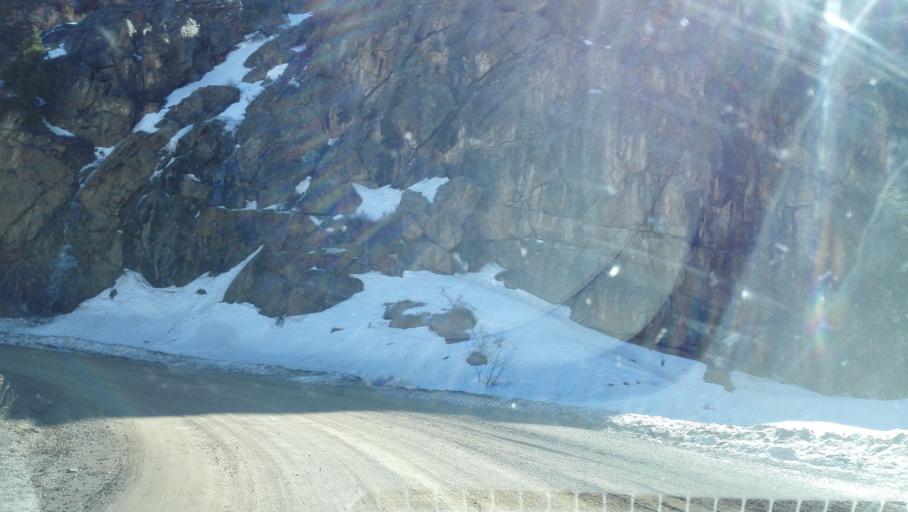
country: US
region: Colorado
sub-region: Hinsdale County
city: Lake City
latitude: 38.4437
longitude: -107.3438
